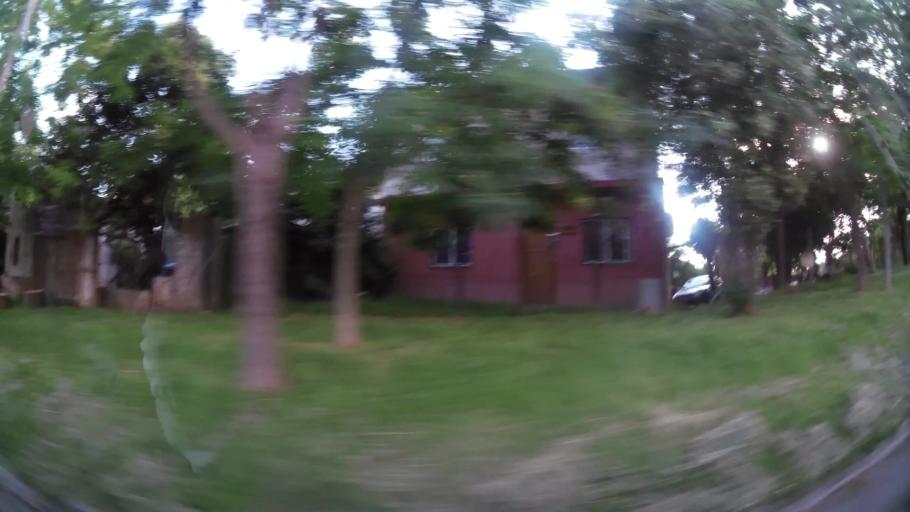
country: AR
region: Buenos Aires
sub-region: Partido de Tigre
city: Tigre
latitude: -34.4703
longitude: -58.6285
